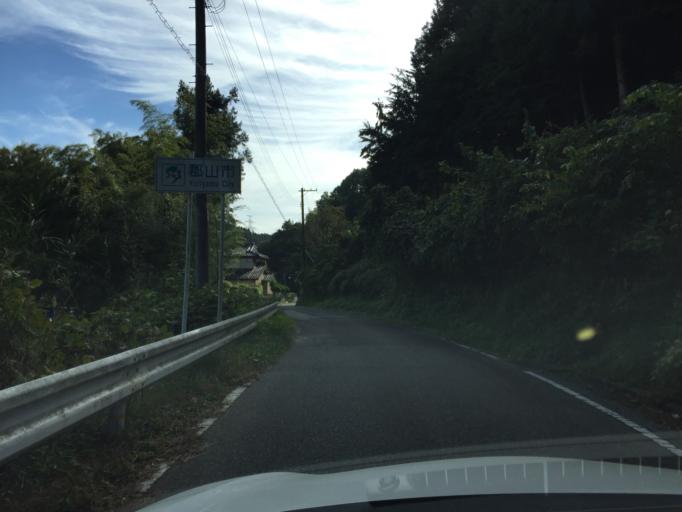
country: JP
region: Fukushima
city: Miharu
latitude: 37.3858
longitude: 140.4530
